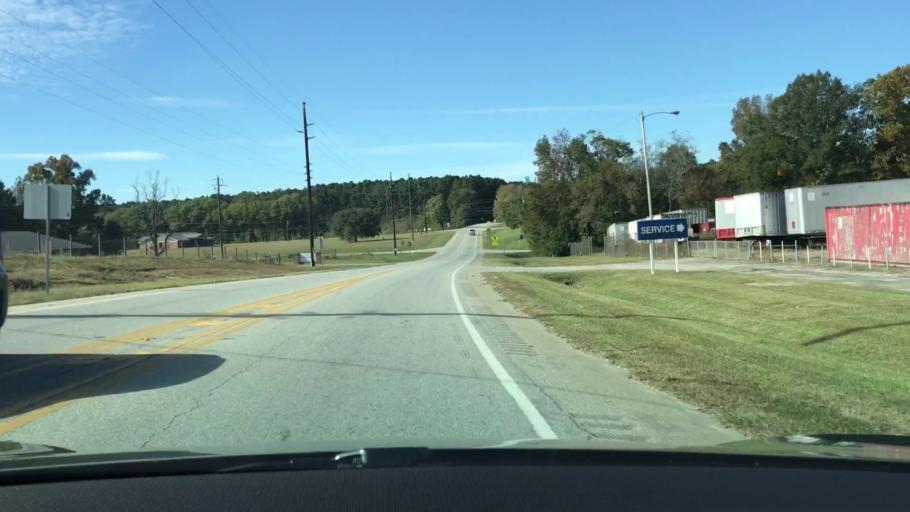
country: US
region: Georgia
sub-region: Warren County
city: Warrenton
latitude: 33.4009
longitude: -82.6569
